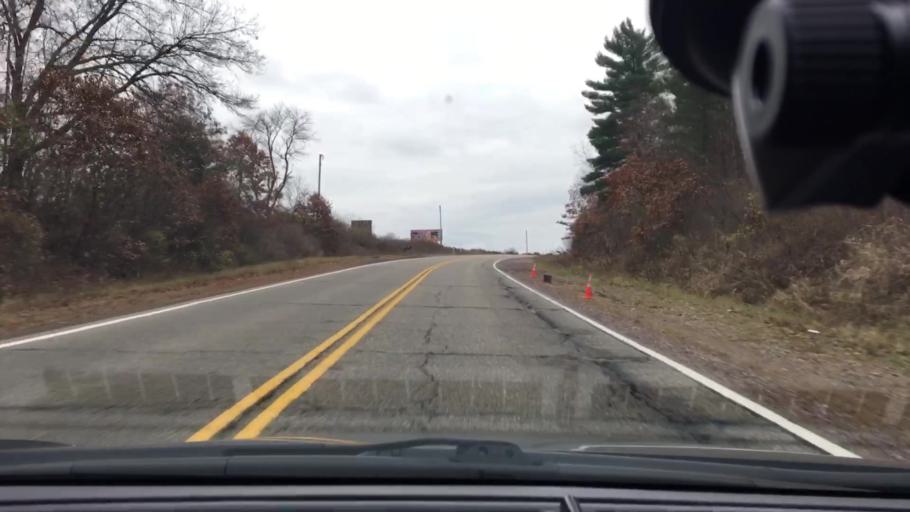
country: US
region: Wisconsin
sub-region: Columbia County
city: Wisconsin Dells
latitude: 43.6395
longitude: -89.7988
